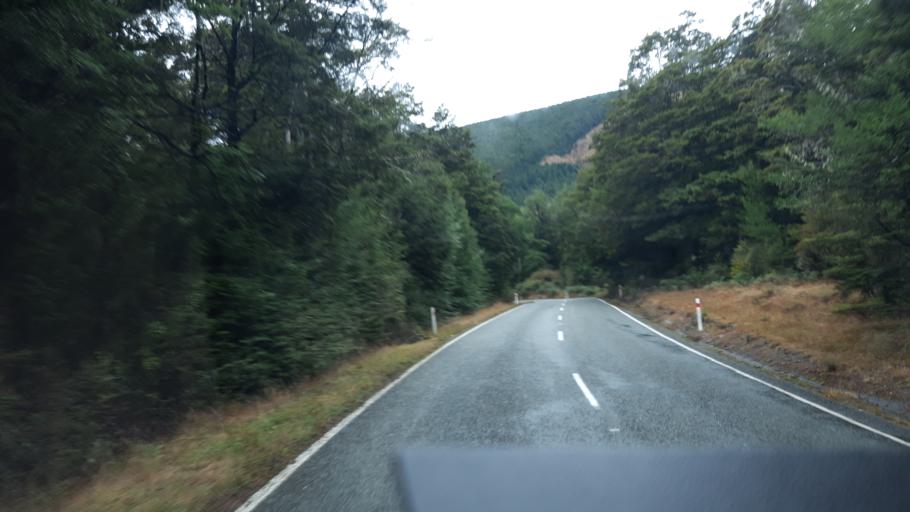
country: NZ
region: Tasman
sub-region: Tasman District
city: Wakefield
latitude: -41.7604
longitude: 172.8973
